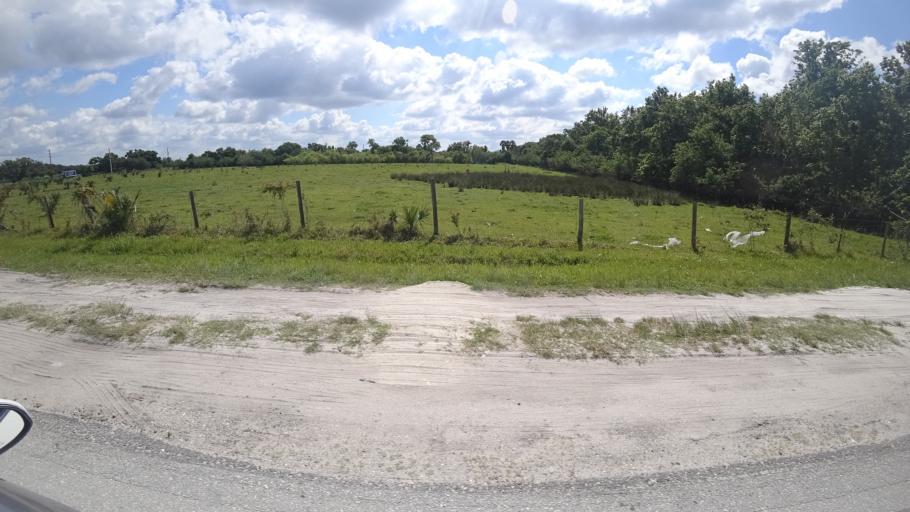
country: US
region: Florida
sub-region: Manatee County
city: Whitfield
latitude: 27.4165
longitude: -82.5282
